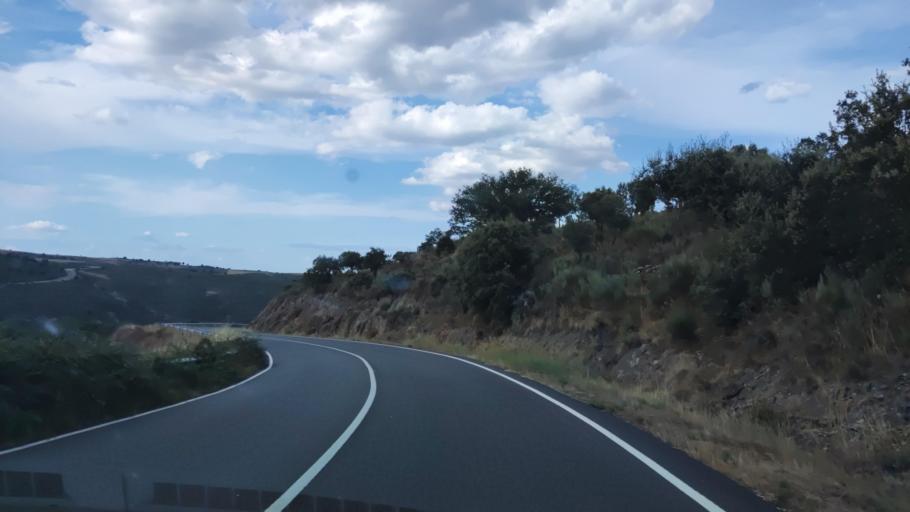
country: ES
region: Castille and Leon
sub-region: Provincia de Salamanca
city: Pastores
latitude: 40.4915
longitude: -6.4963
